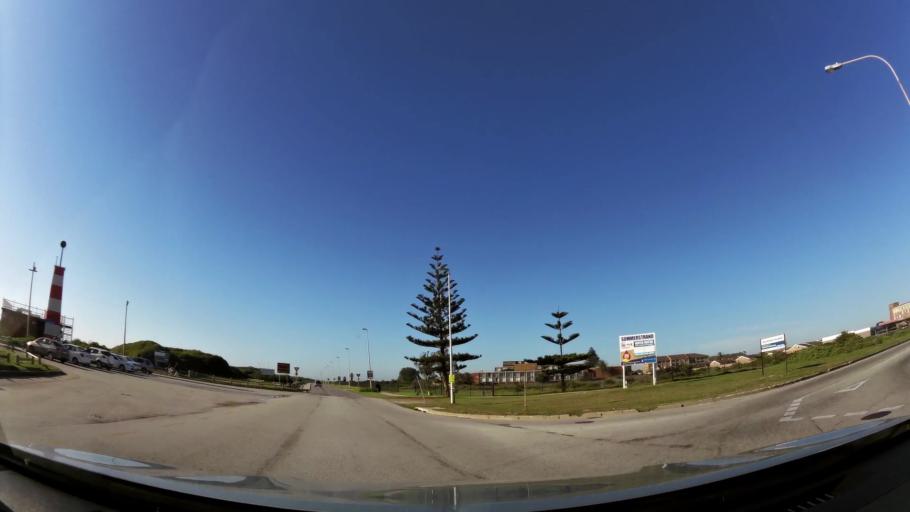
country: ZA
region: Eastern Cape
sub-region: Nelson Mandela Bay Metropolitan Municipality
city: Port Elizabeth
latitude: -33.9912
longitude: 25.6754
